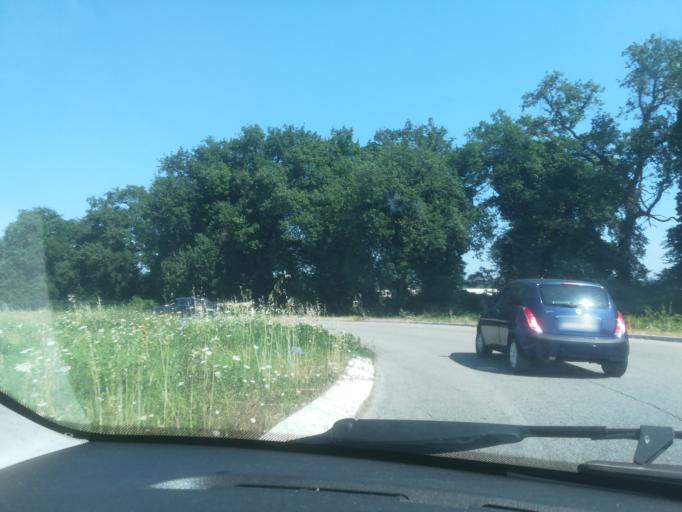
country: IT
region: The Marches
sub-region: Provincia di Macerata
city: Villa Potenza
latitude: 43.3330
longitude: 13.4392
